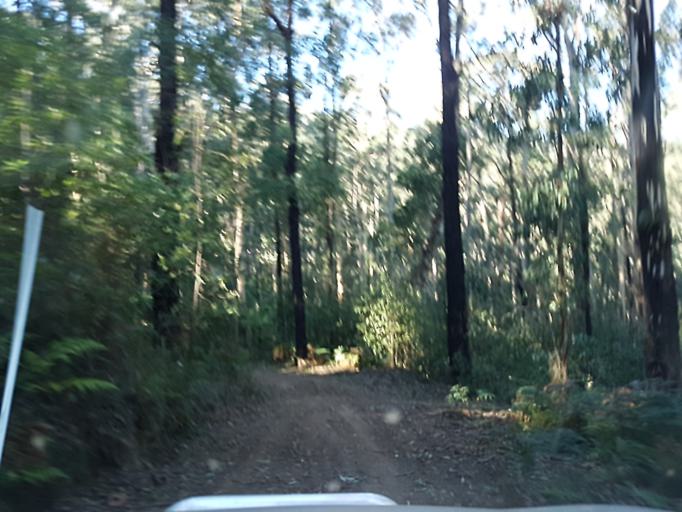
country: AU
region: Victoria
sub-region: Yarra Ranges
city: Healesville
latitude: -37.5800
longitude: 145.4873
